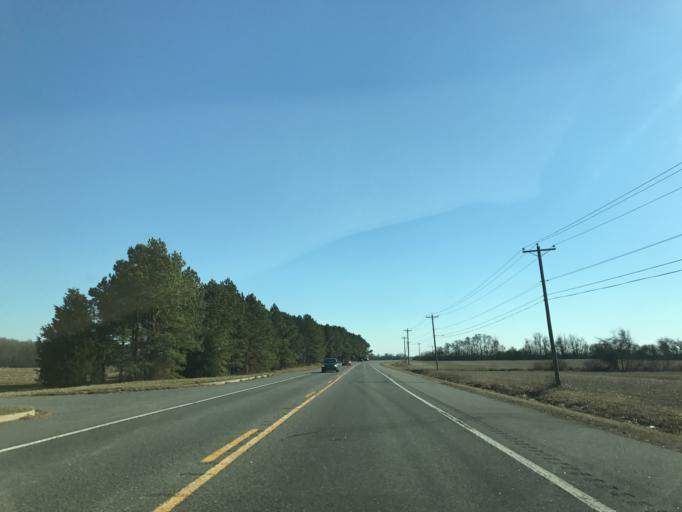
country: US
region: Maryland
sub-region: Queen Anne's County
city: Centreville
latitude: 38.9807
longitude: -76.0706
